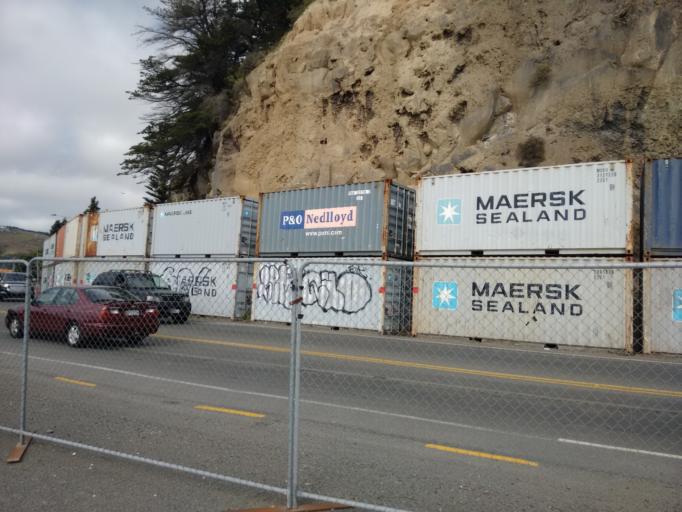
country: NZ
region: Canterbury
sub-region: Christchurch City
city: Christchurch
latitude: -43.5647
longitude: 172.7541
